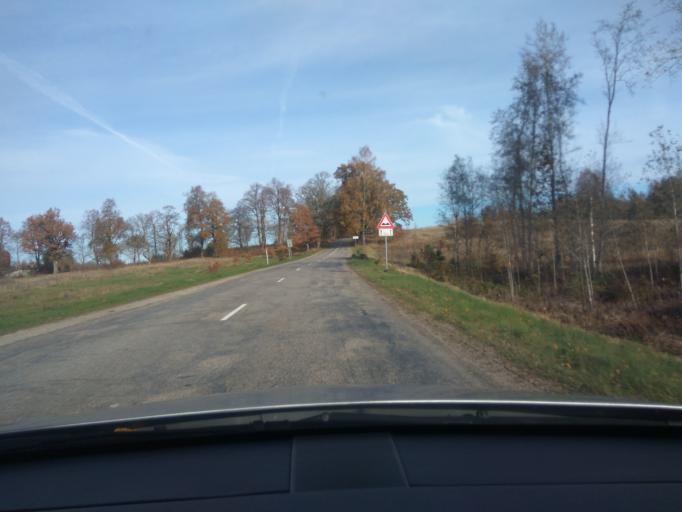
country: LV
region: Alsunga
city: Alsunga
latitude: 57.0106
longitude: 21.6824
